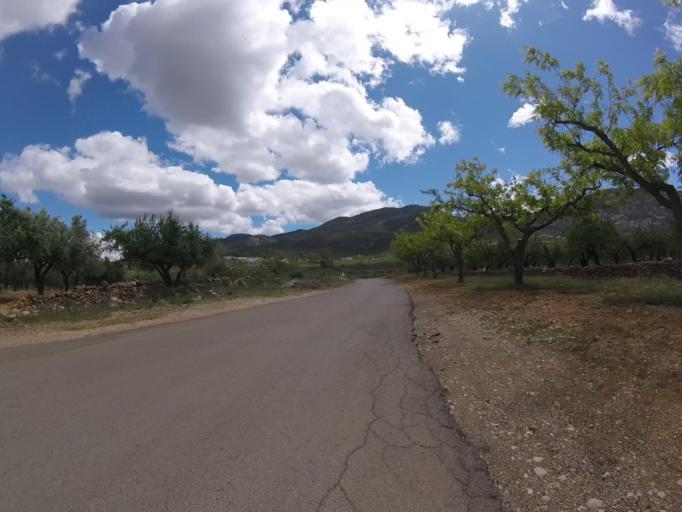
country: ES
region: Valencia
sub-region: Provincia de Castello
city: Sierra-Engarceran
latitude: 40.2904
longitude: -0.0557
